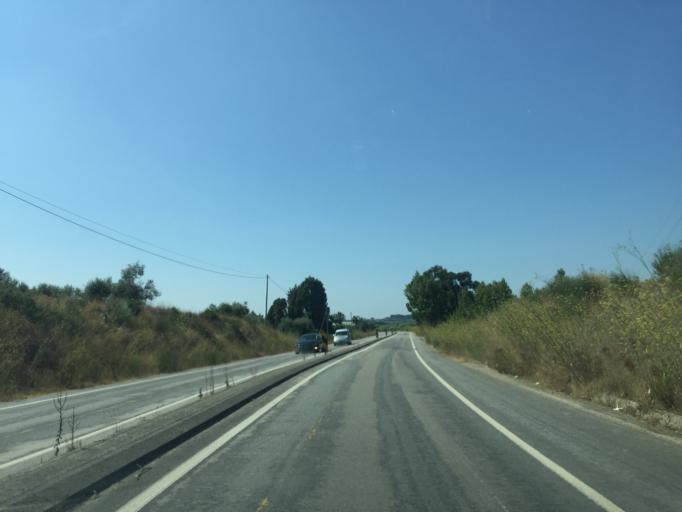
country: PT
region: Aveiro
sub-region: Mealhada
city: Mealhada
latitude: 40.3671
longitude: -8.4579
